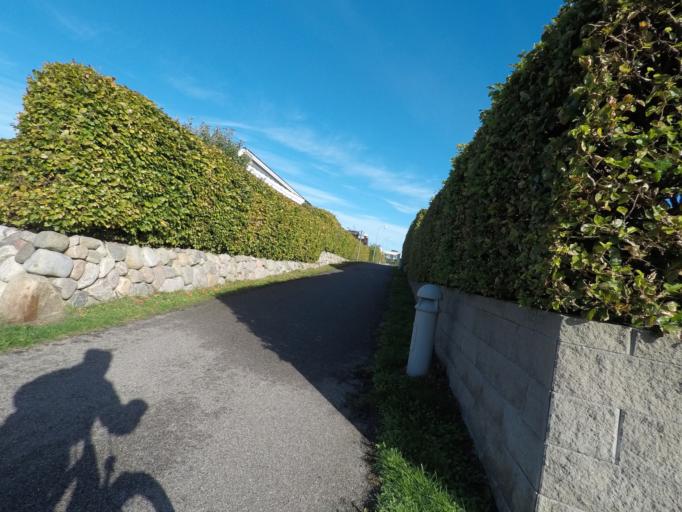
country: DK
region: Capital Region
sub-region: Egedal Kommune
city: Smorumnedre
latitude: 55.7439
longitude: 12.2908
